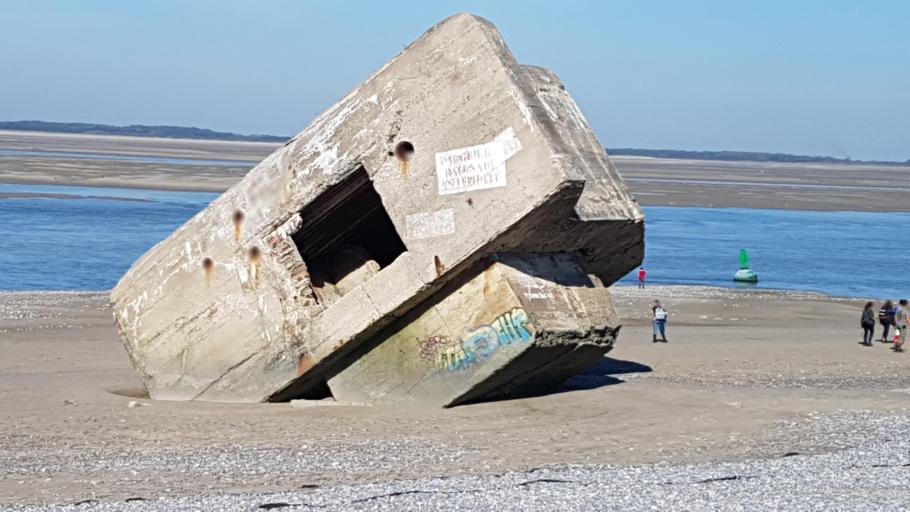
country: FR
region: Picardie
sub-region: Departement de la Somme
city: Pende
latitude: 50.2153
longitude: 1.5519
